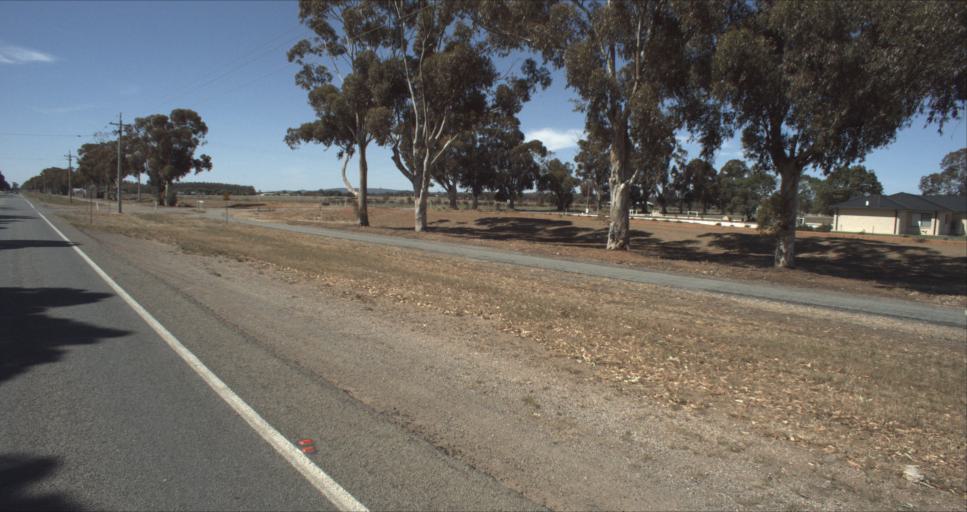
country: AU
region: New South Wales
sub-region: Leeton
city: Leeton
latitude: -34.5933
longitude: 146.4133
